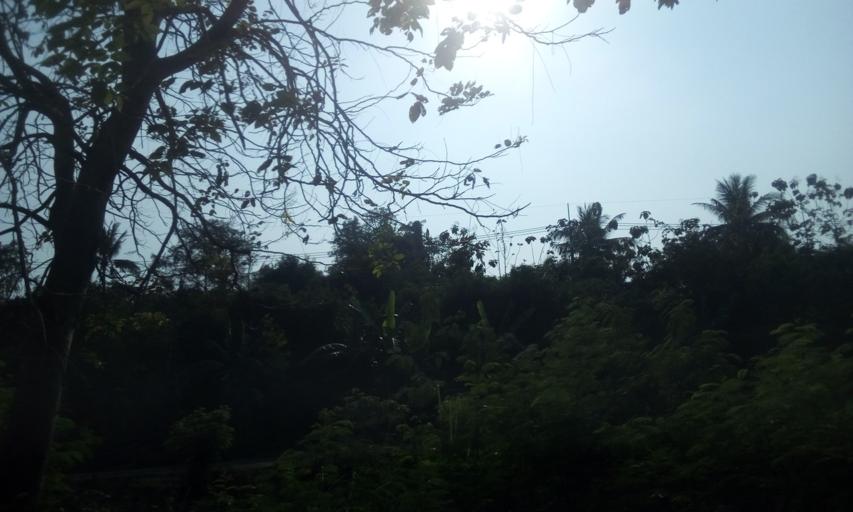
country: TH
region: Sing Buri
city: Phrom Buri
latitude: 14.7518
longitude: 100.4393
